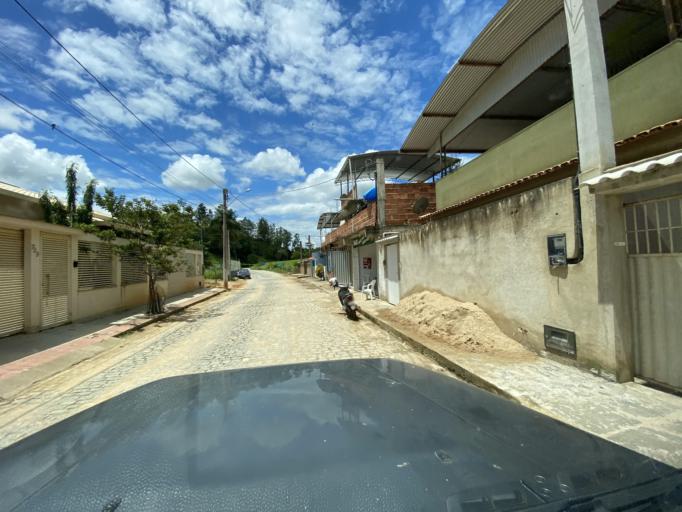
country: BR
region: Espirito Santo
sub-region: Jeronimo Monteiro
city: Jeronimo Monteiro
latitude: -20.7820
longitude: -41.3890
